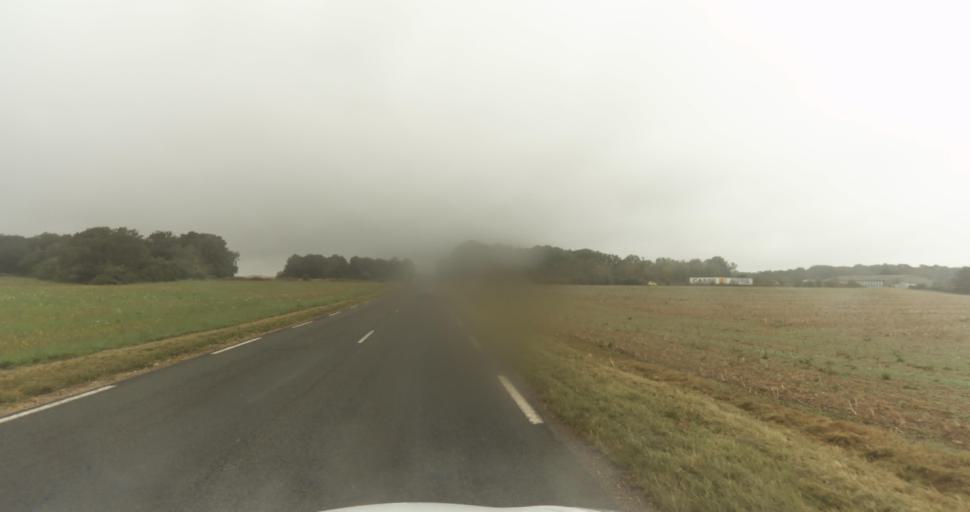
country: FR
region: Haute-Normandie
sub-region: Departement de l'Eure
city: Normanville
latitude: 49.0959
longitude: 1.1751
